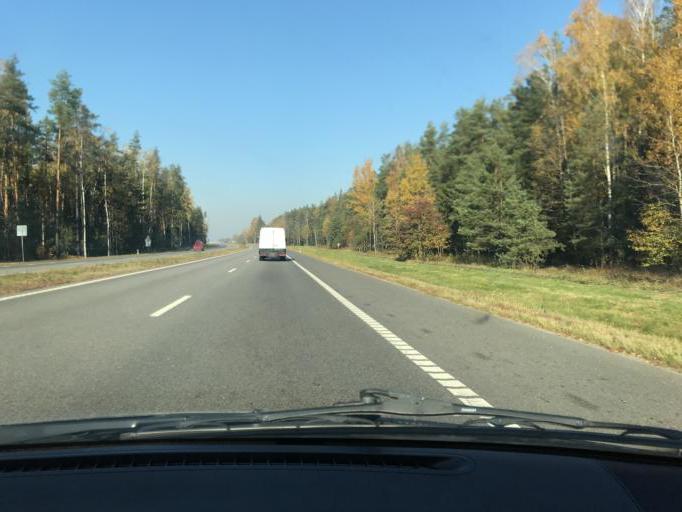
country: BY
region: Minsk
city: Slutsk
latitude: 53.3343
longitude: 27.5288
